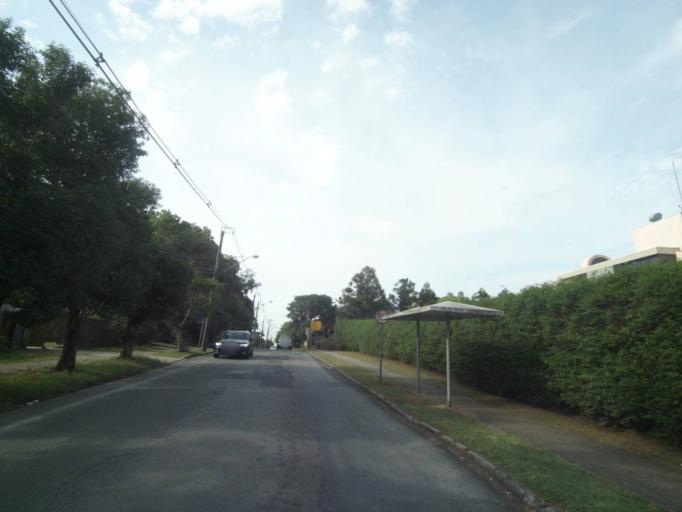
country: BR
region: Parana
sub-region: Curitiba
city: Curitiba
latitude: -25.4216
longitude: -49.3196
